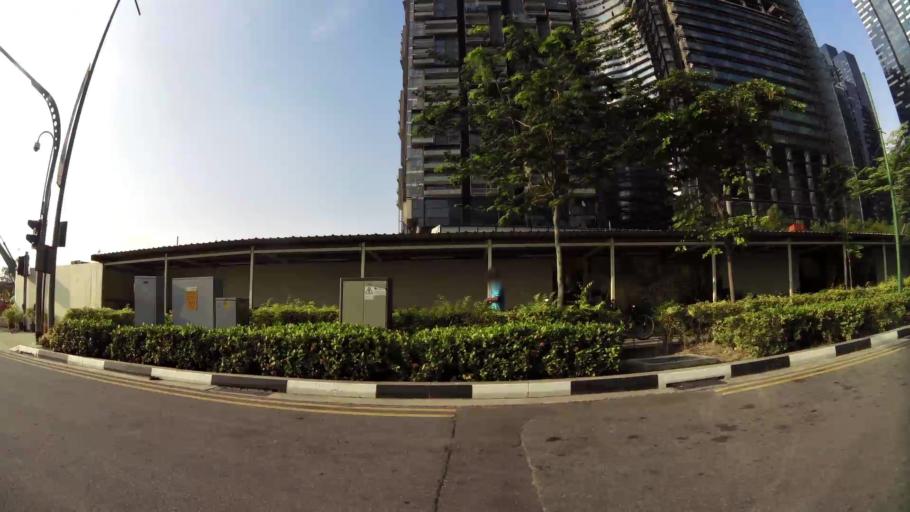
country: SG
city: Singapore
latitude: 1.2784
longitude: 103.8544
